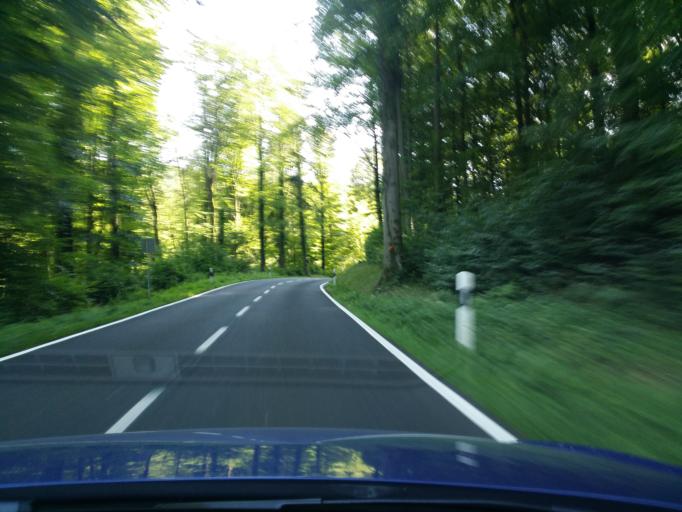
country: LU
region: Luxembourg
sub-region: Canton de Capellen
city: Kopstal
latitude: 49.6461
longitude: 6.0534
